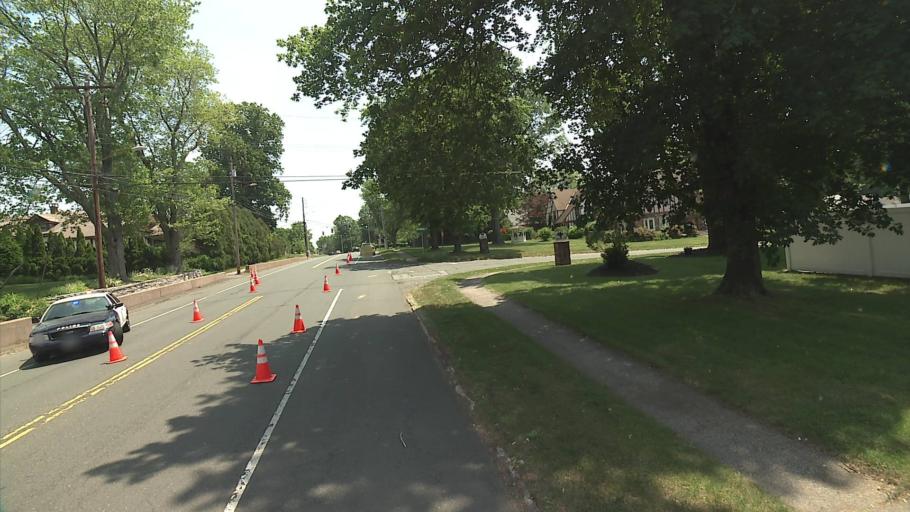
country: US
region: Connecticut
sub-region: Hartford County
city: East Hartford
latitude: 41.7661
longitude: -72.5929
